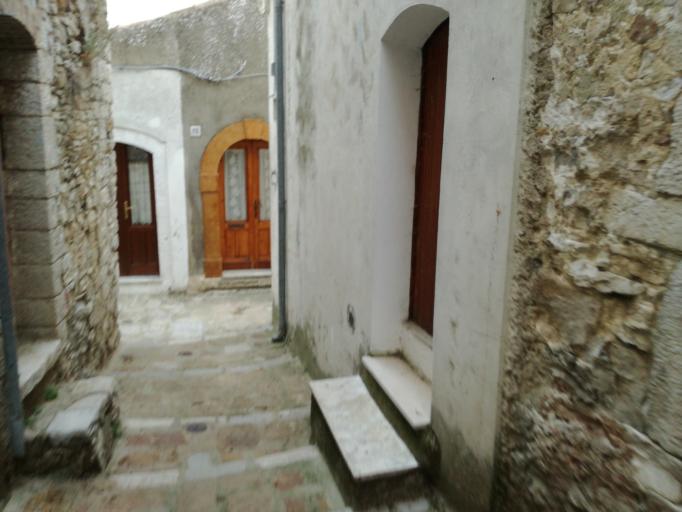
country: IT
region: Basilicate
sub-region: Provincia di Potenza
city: Pietragalla
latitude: 40.7473
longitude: 15.8806
